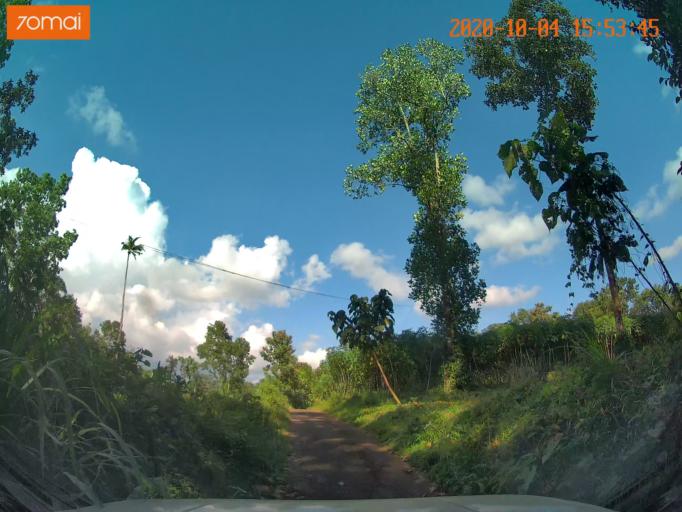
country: IN
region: Kerala
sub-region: Kottayam
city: Palackattumala
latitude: 9.7821
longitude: 76.5577
